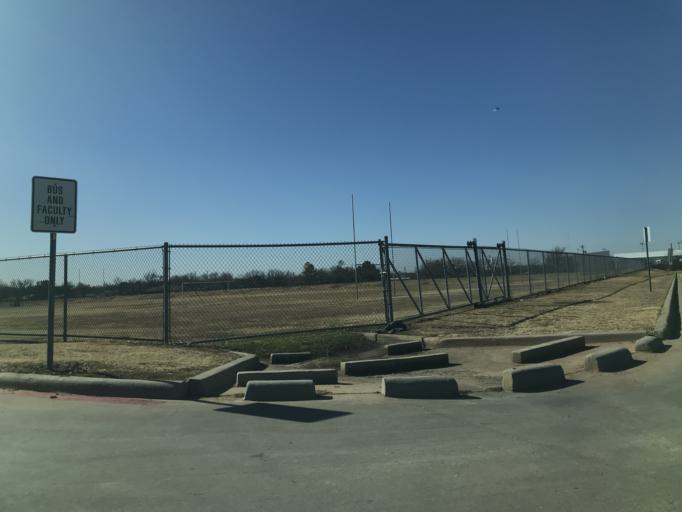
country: US
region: Texas
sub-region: Taylor County
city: Abilene
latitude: 32.4423
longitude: -99.7083
